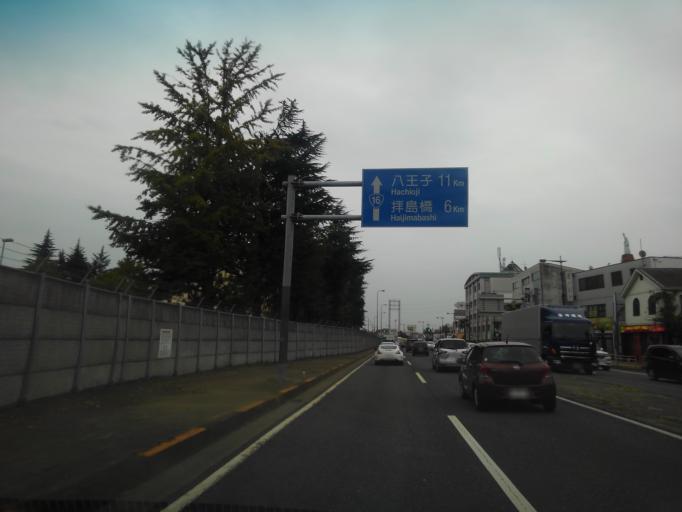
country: JP
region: Tokyo
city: Fussa
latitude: 35.7417
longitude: 139.3381
